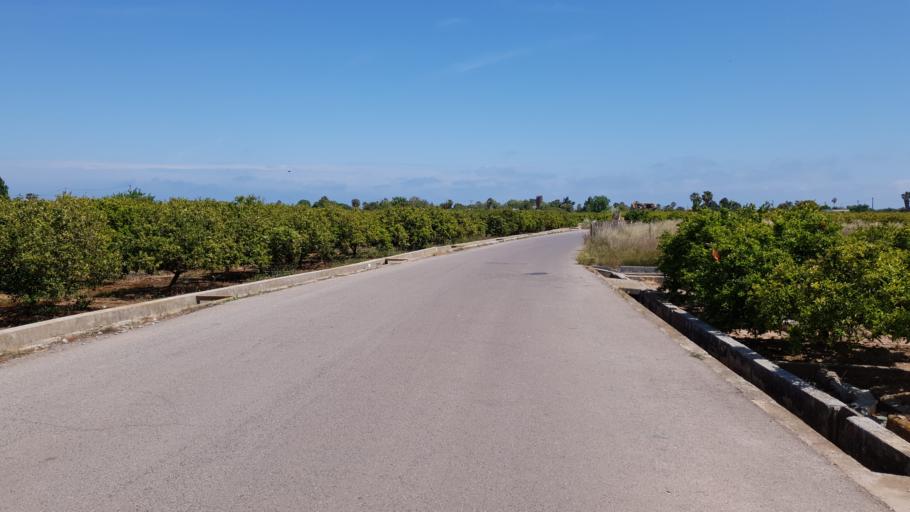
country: ES
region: Valencia
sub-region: Provincia de Castello
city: Burriana
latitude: 39.8624
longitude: -0.0895
